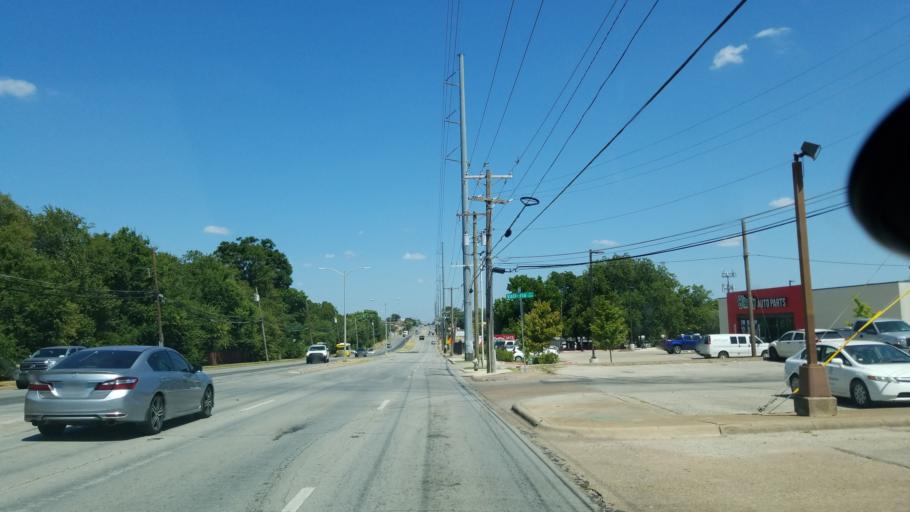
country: US
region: Texas
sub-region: Dallas County
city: Cockrell Hill
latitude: 32.7203
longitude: -96.8859
